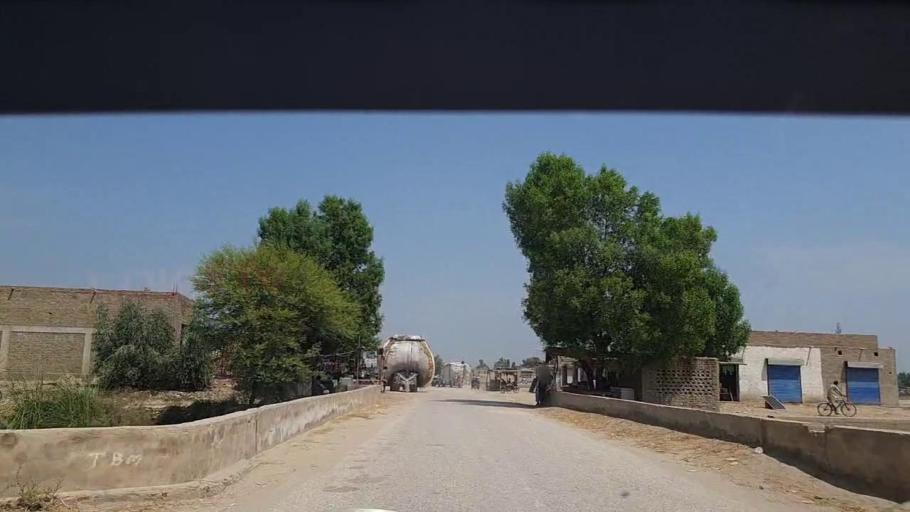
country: PK
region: Sindh
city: Thul
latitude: 28.1169
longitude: 68.8119
